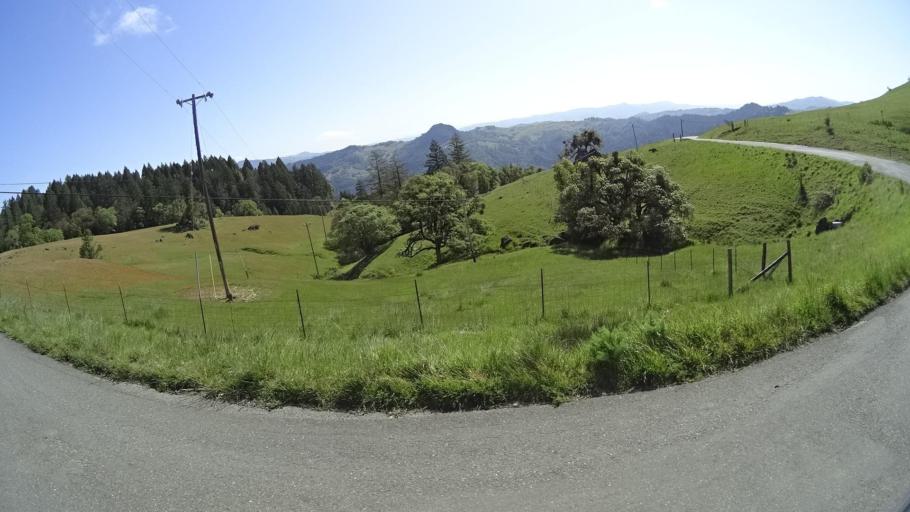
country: US
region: California
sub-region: Humboldt County
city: Redway
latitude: 40.0812
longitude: -123.6558
